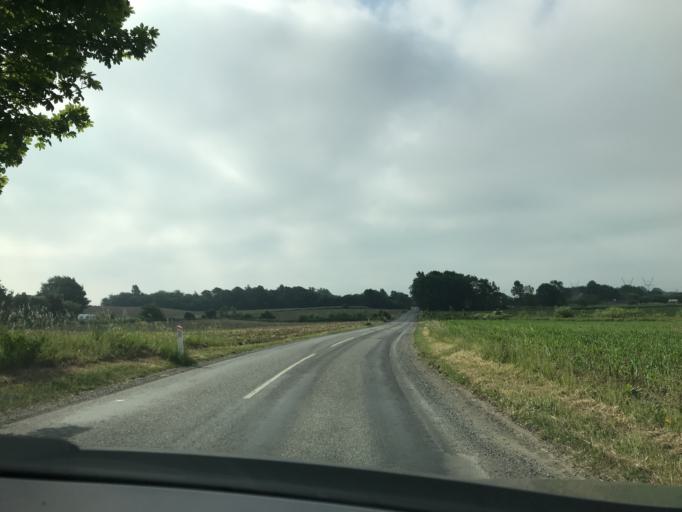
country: DK
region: South Denmark
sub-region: Odense Kommune
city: Bellinge
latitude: 55.3739
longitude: 10.2935
